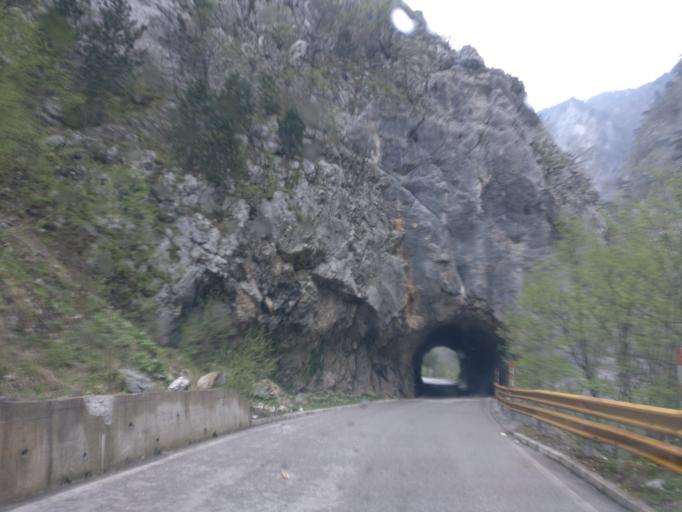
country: ME
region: Opstina Pluzine
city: Pluzine
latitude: 43.2769
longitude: 18.8480
